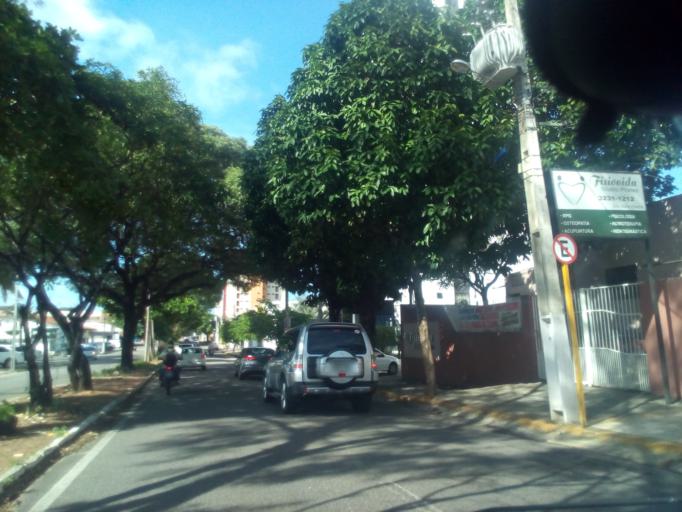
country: BR
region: Rio Grande do Norte
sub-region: Natal
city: Natal
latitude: -5.8205
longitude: -35.2156
